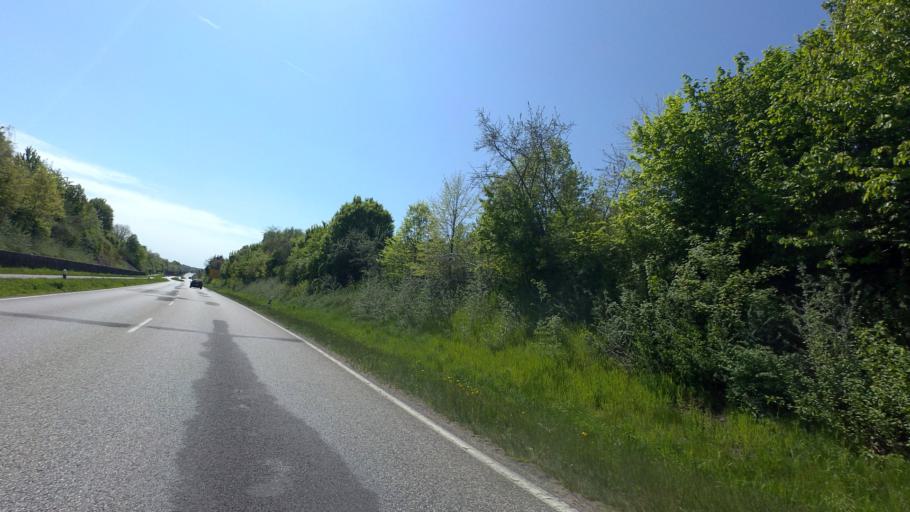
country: DE
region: Brandenburg
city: Konigs Wusterhausen
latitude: 52.2979
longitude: 13.6018
